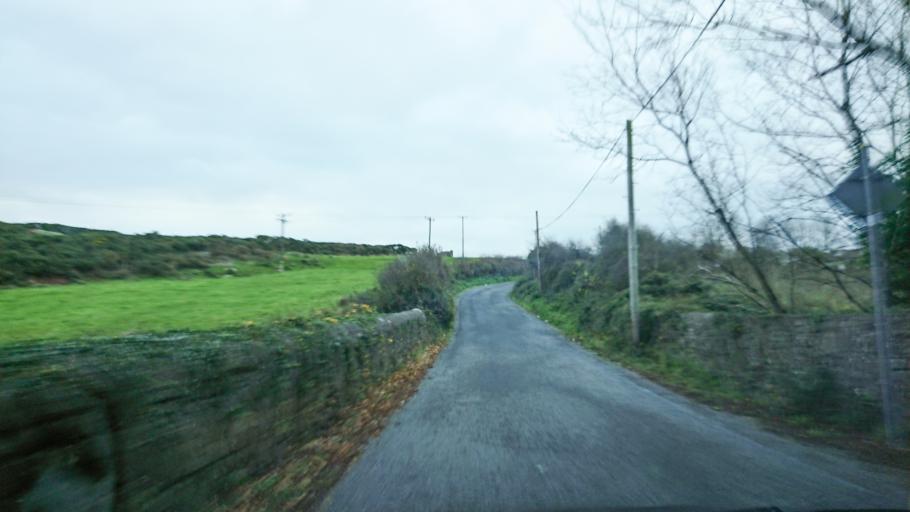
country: IE
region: Munster
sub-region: Waterford
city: Dunmore East
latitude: 52.2377
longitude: -6.9761
